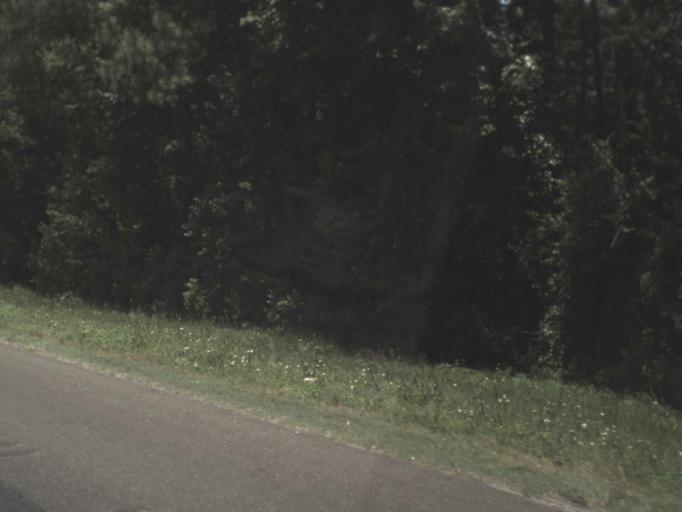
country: US
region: Florida
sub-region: Duval County
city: Jacksonville
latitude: 30.4602
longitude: -81.6711
